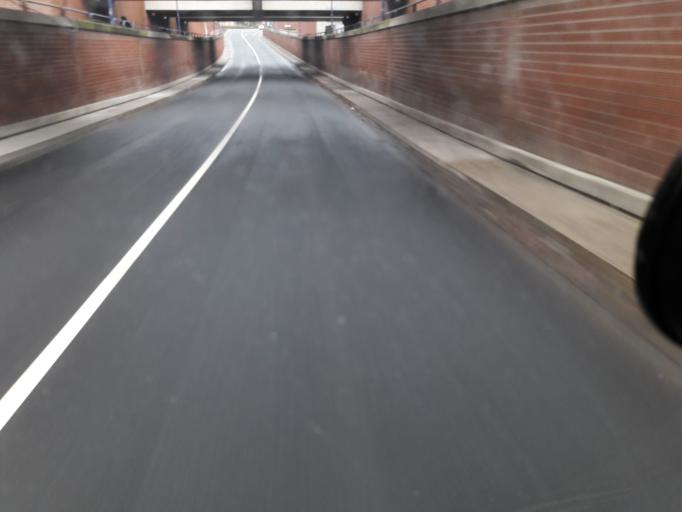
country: DE
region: Lower Saxony
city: Bad Bentheim
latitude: 52.3106
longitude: 7.1593
